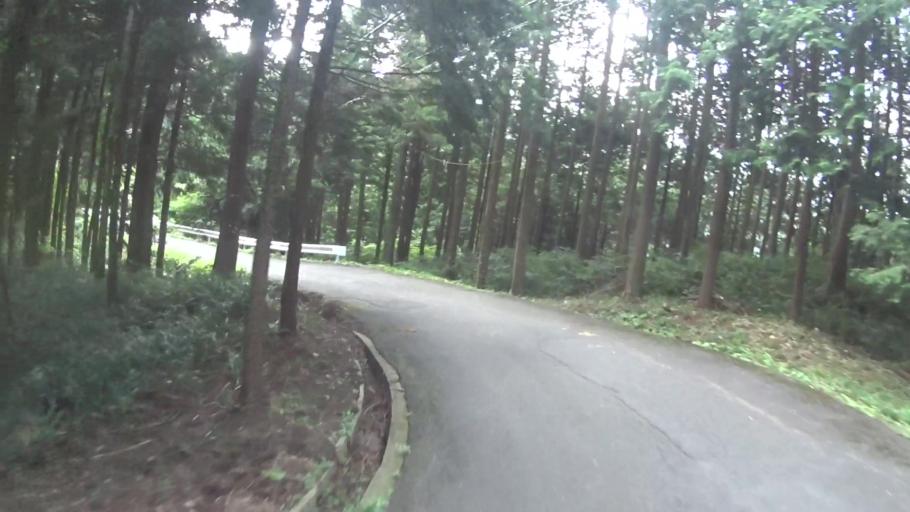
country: JP
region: Kyoto
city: Miyazu
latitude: 35.7374
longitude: 135.1922
